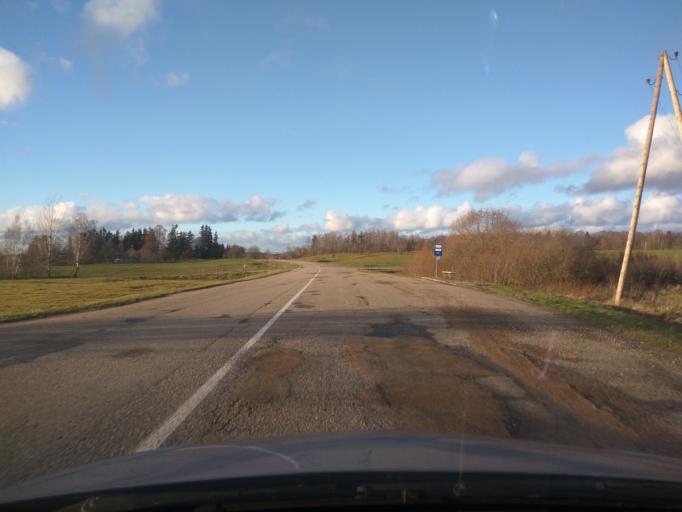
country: LV
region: Aizpute
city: Aizpute
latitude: 56.7494
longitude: 21.5712
